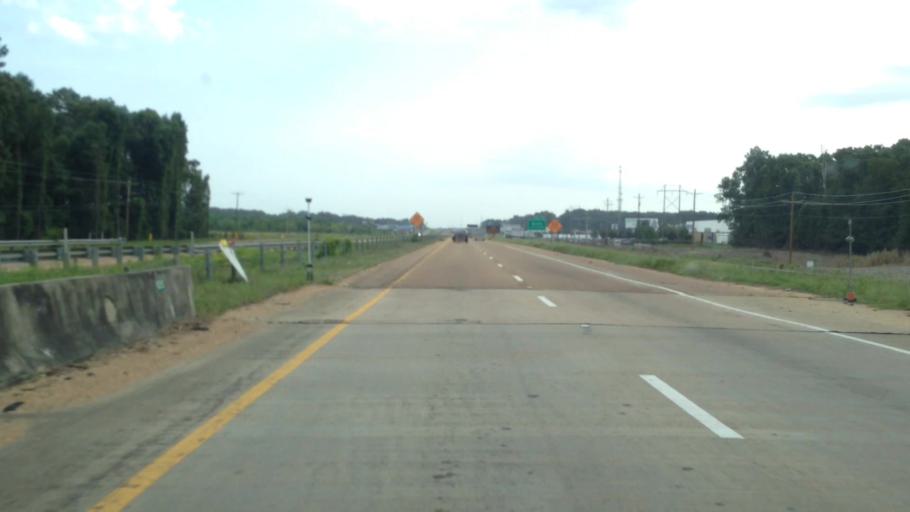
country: US
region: Mississippi
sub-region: Hinds County
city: Byram
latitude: 32.1641
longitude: -90.2698
